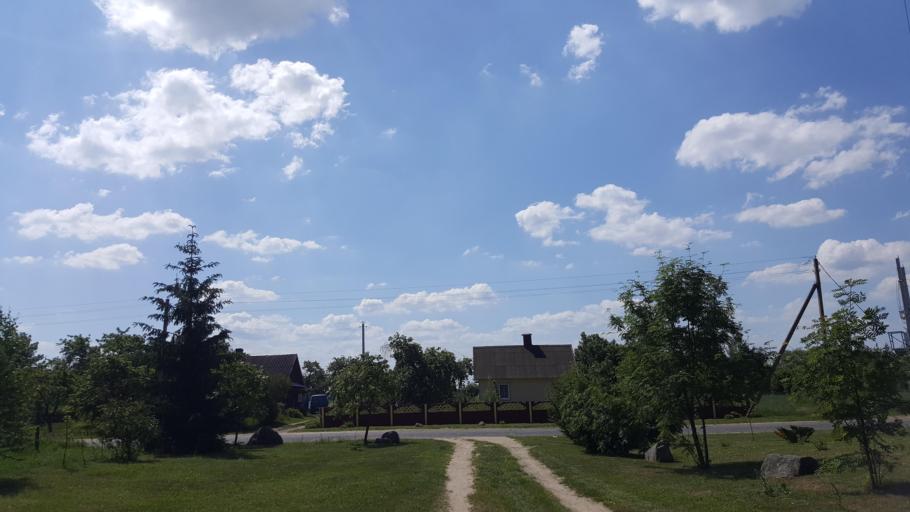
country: BY
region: Brest
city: Zhabinka
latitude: 52.2437
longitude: 24.0266
